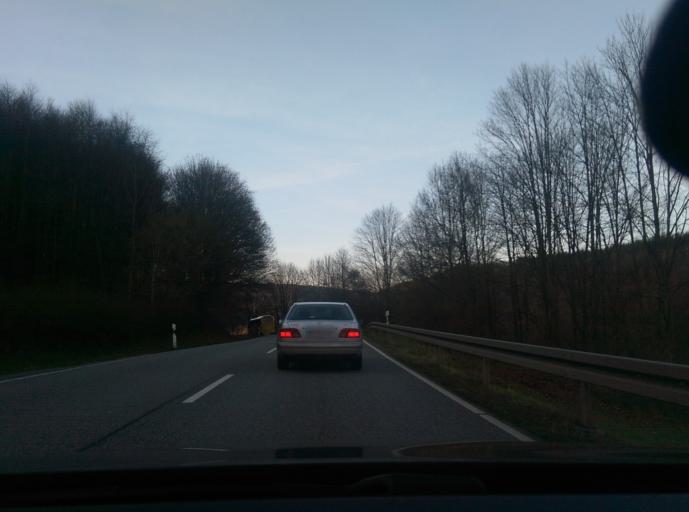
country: DE
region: Hesse
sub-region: Regierungsbezirk Kassel
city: Sontra
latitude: 51.0949
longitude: 9.9738
